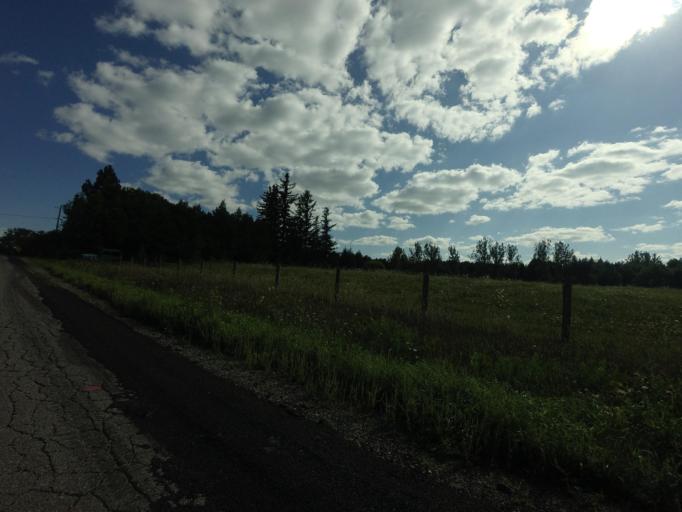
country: CA
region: Ontario
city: Orangeville
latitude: 43.8271
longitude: -79.9995
